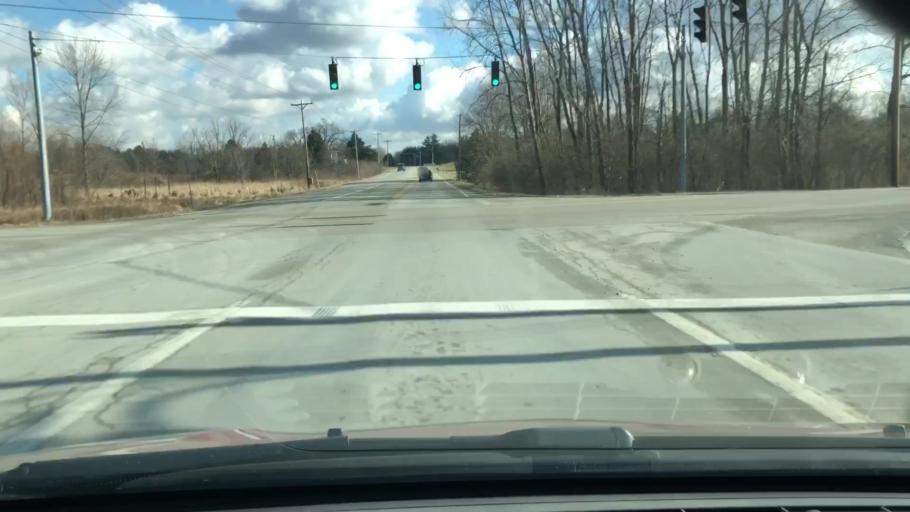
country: US
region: Ohio
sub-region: Greene County
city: Fairborn
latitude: 39.7889
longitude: -83.9636
